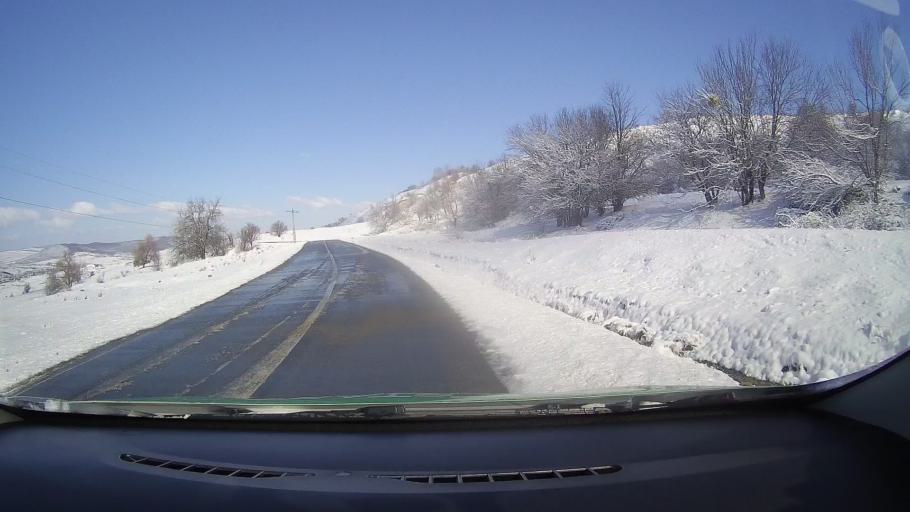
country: RO
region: Sibiu
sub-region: Comuna Avrig
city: Avrig
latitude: 45.7828
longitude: 24.3746
